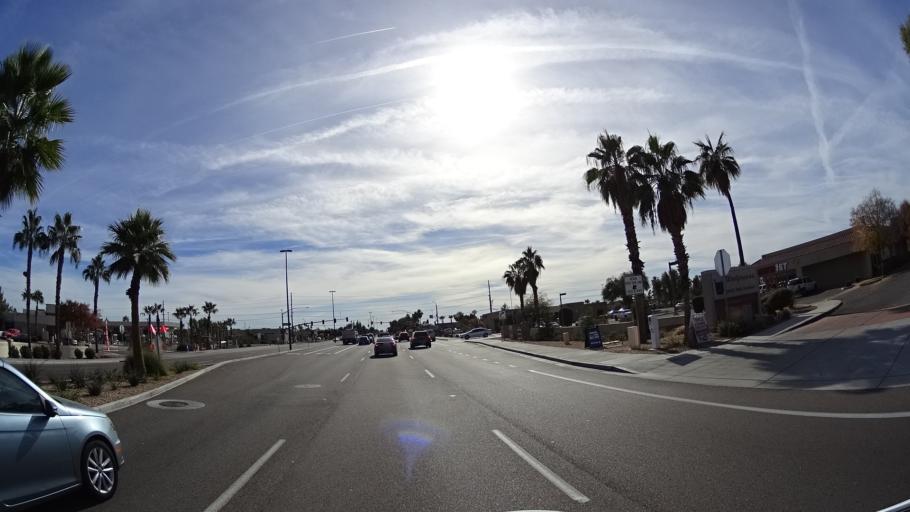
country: US
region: Arizona
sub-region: Maricopa County
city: Gilbert
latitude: 33.3659
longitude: -111.7900
